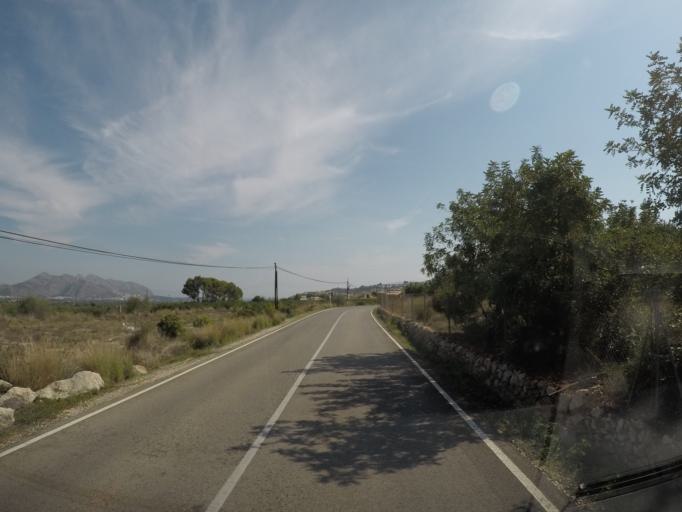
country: ES
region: Valencia
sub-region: Provincia de Alicante
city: Orba
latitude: 38.7813
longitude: -0.0759
